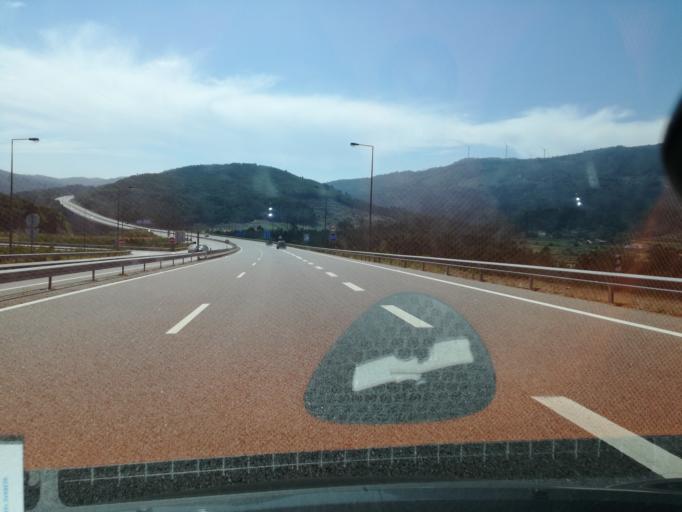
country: PT
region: Viana do Castelo
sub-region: Caminha
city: Vila Praia de Ancora
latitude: 41.8049
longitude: -8.8029
